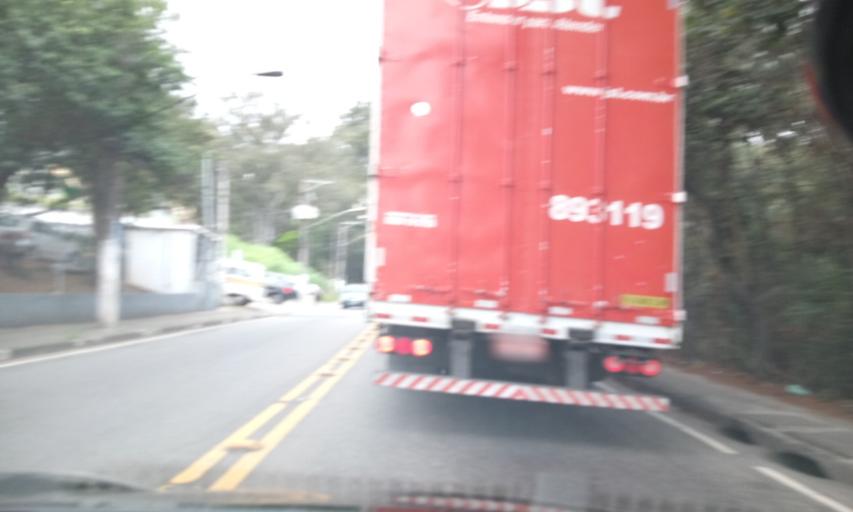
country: BR
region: Sao Paulo
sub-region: Sao Caetano Do Sul
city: Sao Caetano do Sul
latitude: -23.6494
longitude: -46.5842
